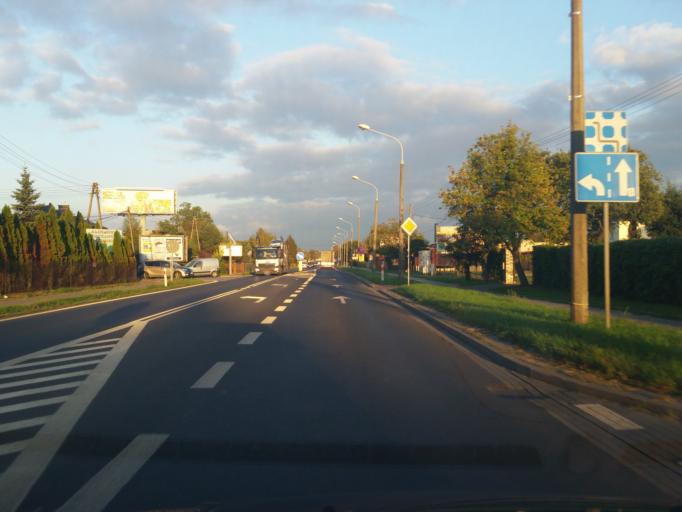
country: PL
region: Masovian Voivodeship
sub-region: Powiat warszawski zachodni
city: Ozarow Mazowiecki
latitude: 52.2109
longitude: 20.7788
